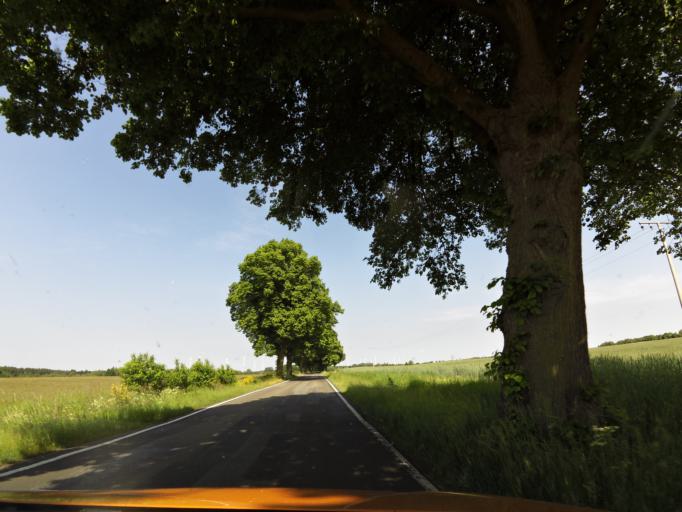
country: DE
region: Mecklenburg-Vorpommern
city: Neuburg
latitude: 53.3977
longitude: 11.9267
